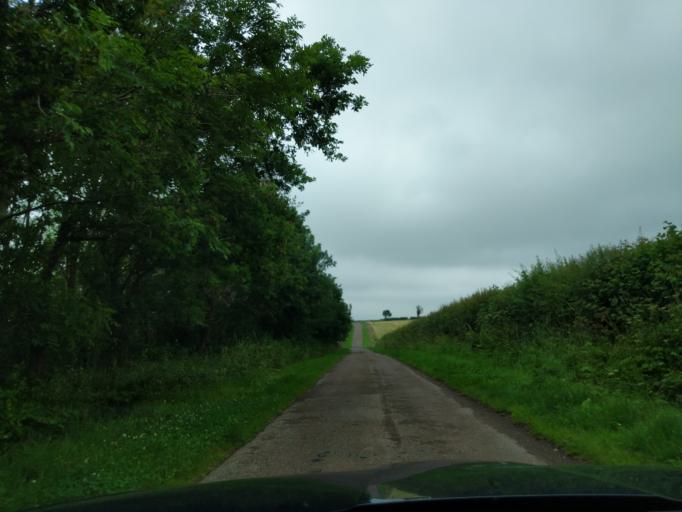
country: GB
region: England
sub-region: Northumberland
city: Ford
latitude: 55.6888
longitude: -2.1275
